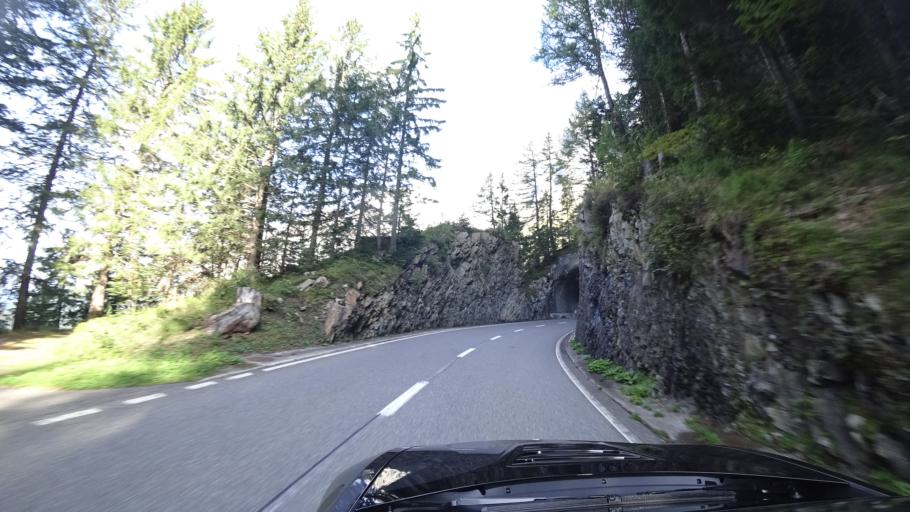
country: CH
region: Obwalden
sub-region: Obwalden
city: Engelberg
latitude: 46.7387
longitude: 8.3810
